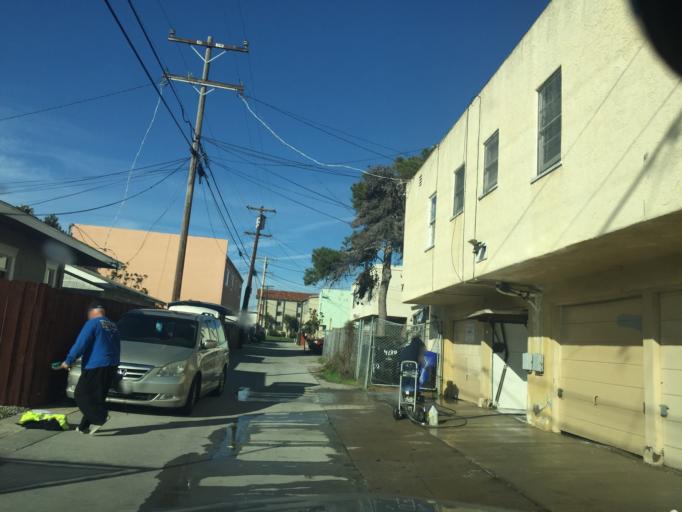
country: US
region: California
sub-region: San Diego County
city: San Diego
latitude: 32.7520
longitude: -117.1199
